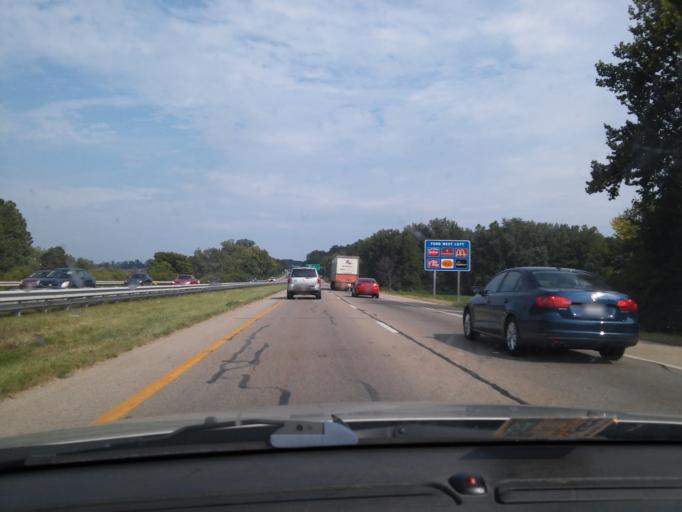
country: US
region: Ohio
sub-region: Greene County
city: Xenia
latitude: 39.6987
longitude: -83.9934
